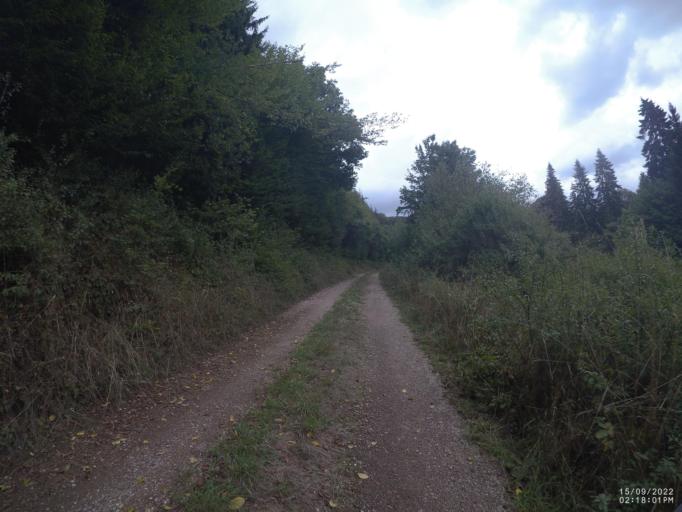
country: DE
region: Rheinland-Pfalz
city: Oberehe-Stroheich
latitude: 50.2890
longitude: 6.7759
